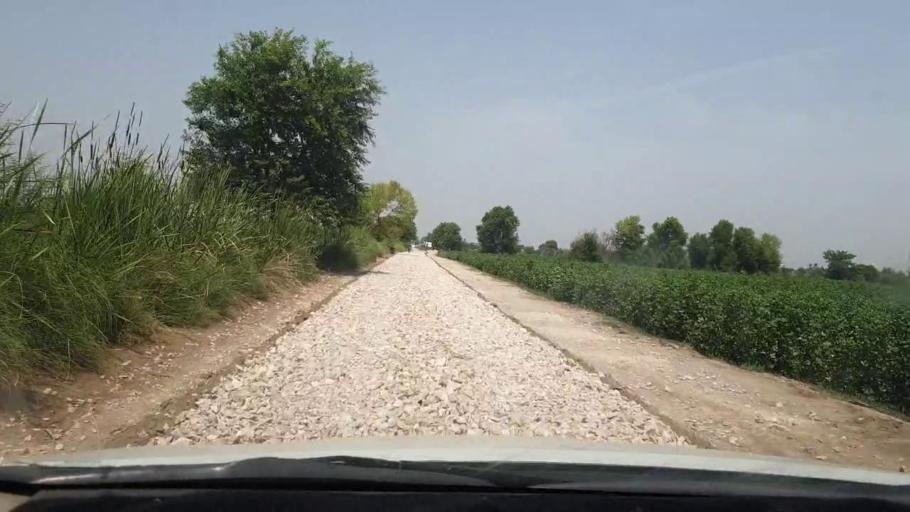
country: PK
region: Sindh
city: Rohri
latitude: 27.4947
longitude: 69.0314
